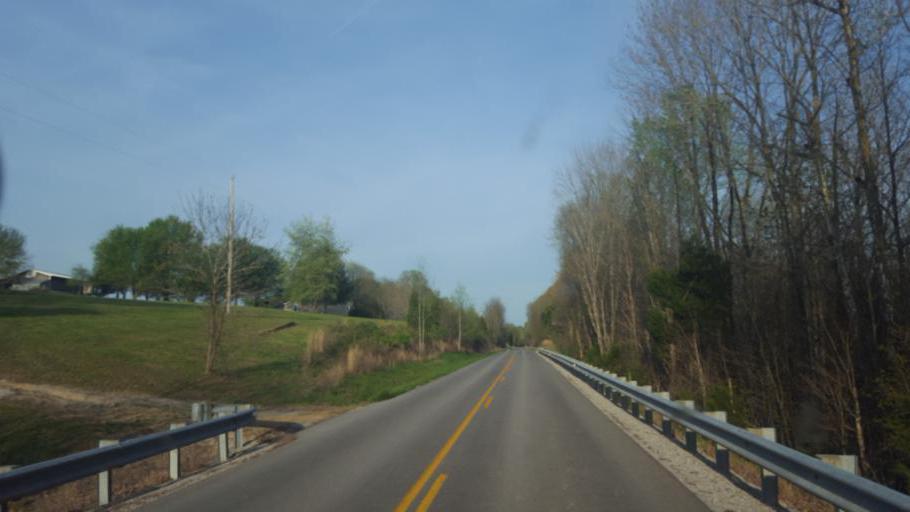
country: US
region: Kentucky
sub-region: Barren County
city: Glasgow
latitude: 36.9430
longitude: -86.0427
